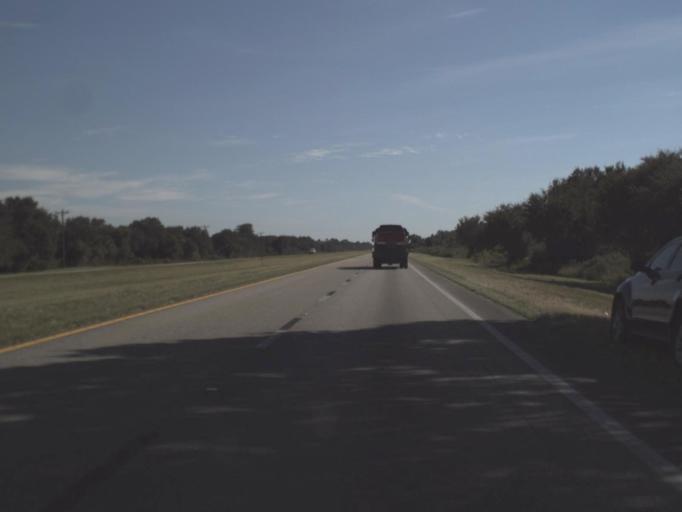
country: US
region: Florida
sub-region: Hendry County
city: Port LaBelle
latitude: 26.9926
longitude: -81.3265
